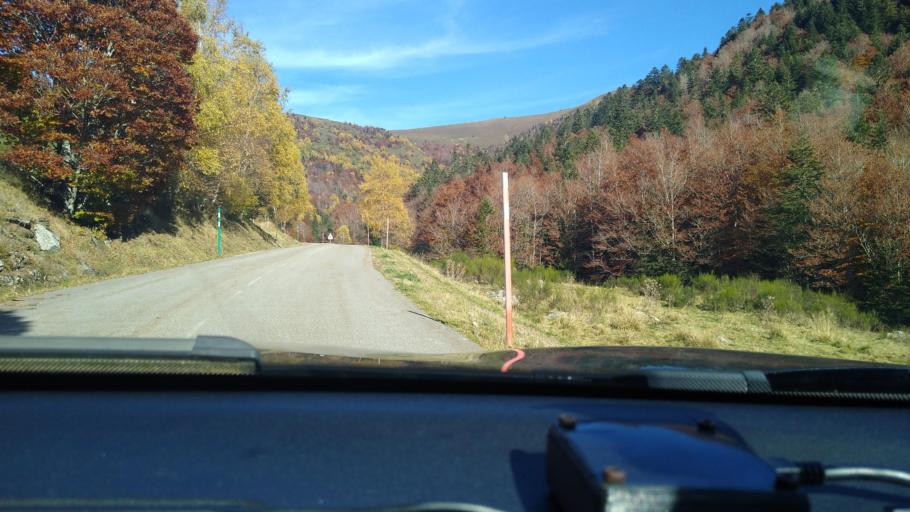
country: FR
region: Midi-Pyrenees
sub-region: Departement de l'Ariege
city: Ax-les-Thermes
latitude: 42.7273
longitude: 1.9462
